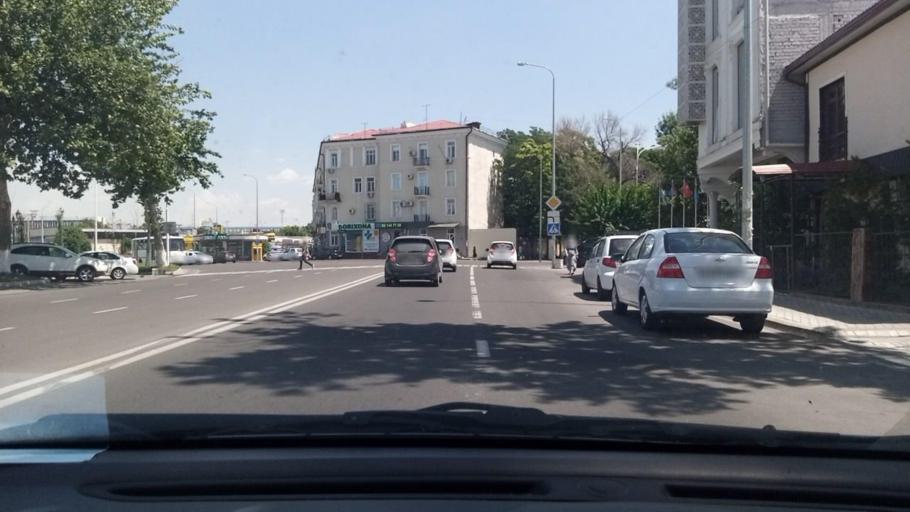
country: UZ
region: Toshkent Shahri
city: Tashkent
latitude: 41.2868
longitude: 69.2823
